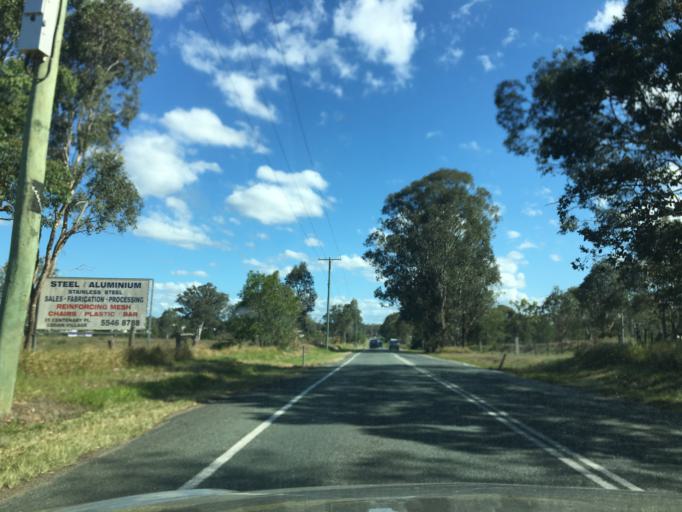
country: AU
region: Queensland
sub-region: Logan
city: Chambers Flat
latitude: -27.7603
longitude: 153.1103
